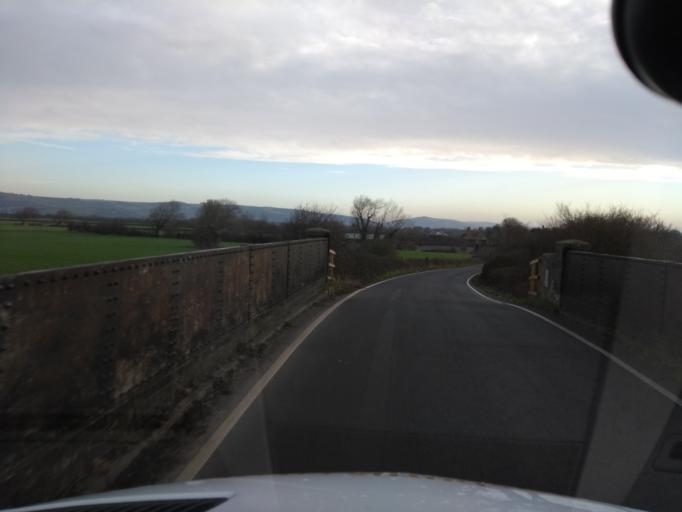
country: GB
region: England
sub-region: North Somerset
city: Bleadon
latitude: 51.2845
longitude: -2.9705
